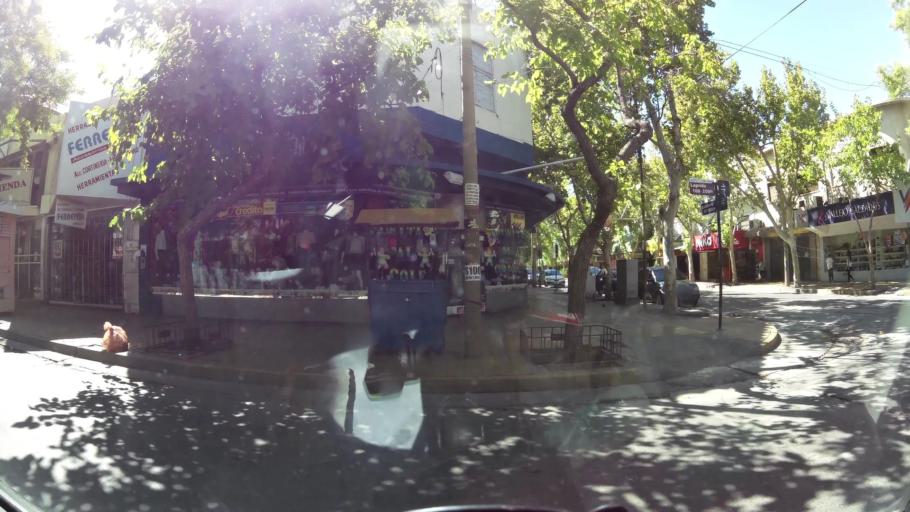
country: AR
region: San Juan
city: San Juan
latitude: -31.5353
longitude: -68.5232
